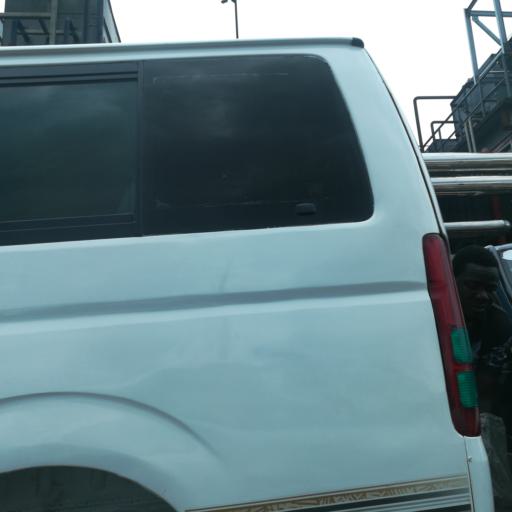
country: NG
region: Rivers
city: Port Harcourt
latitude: 4.8150
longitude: 7.0424
